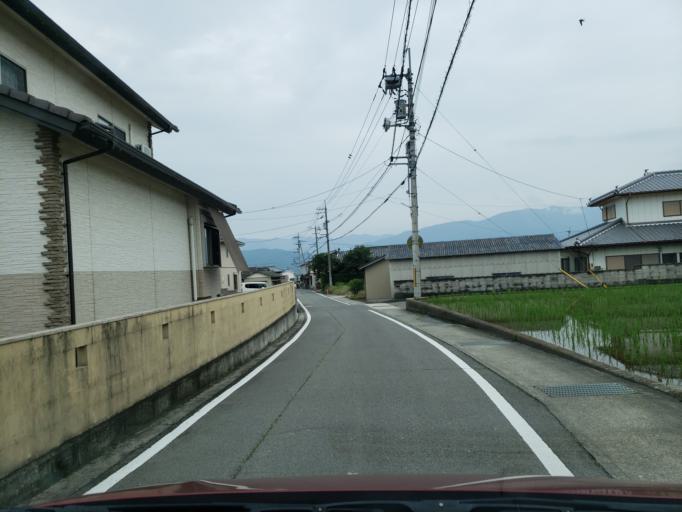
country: JP
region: Tokushima
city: Wakimachi
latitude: 34.0921
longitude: 134.2291
